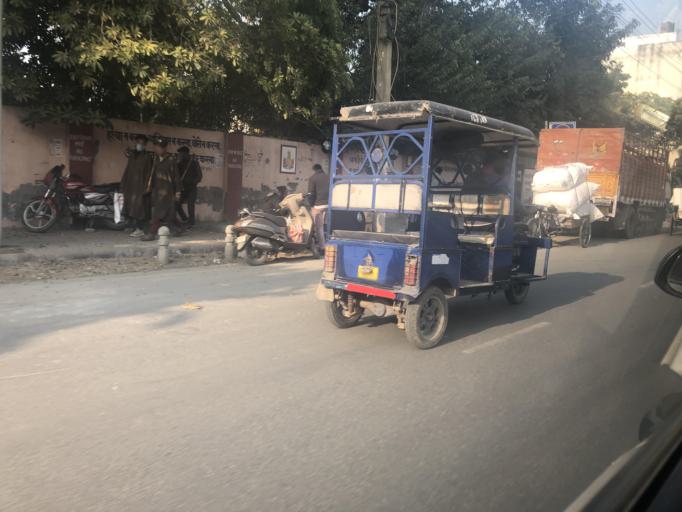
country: IN
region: Haryana
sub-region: Jhajjar
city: Bahadurgarh
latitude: 28.6148
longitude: 76.9816
